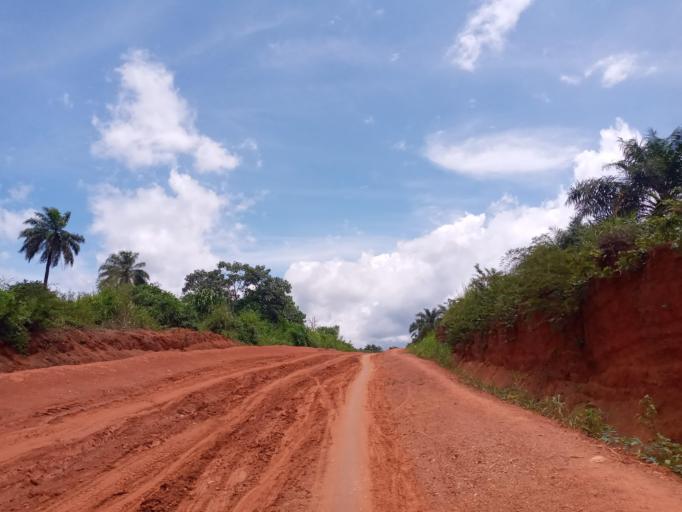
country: SL
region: Eastern Province
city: Koidu
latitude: 8.6449
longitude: -10.9138
